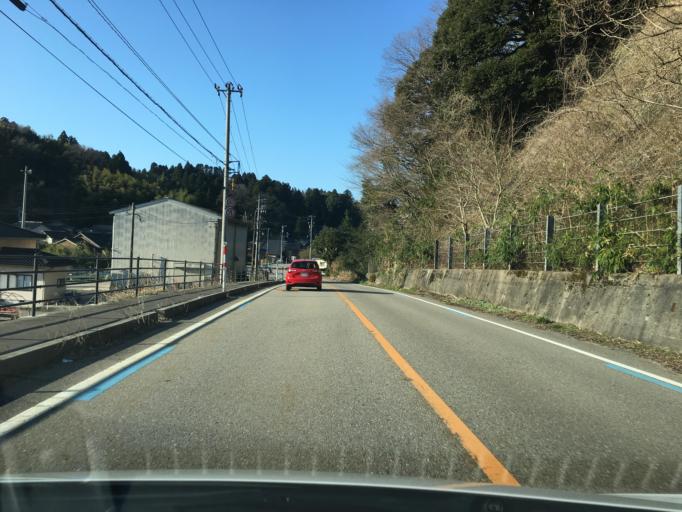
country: JP
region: Toyama
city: Himi
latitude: 36.9304
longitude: 137.0262
